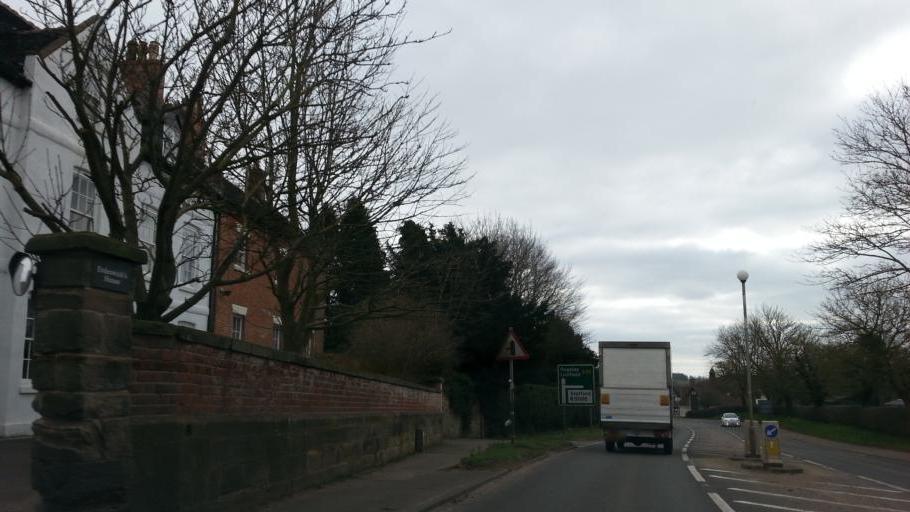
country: GB
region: England
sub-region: Staffordshire
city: Stafford
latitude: 52.8632
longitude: -2.0786
